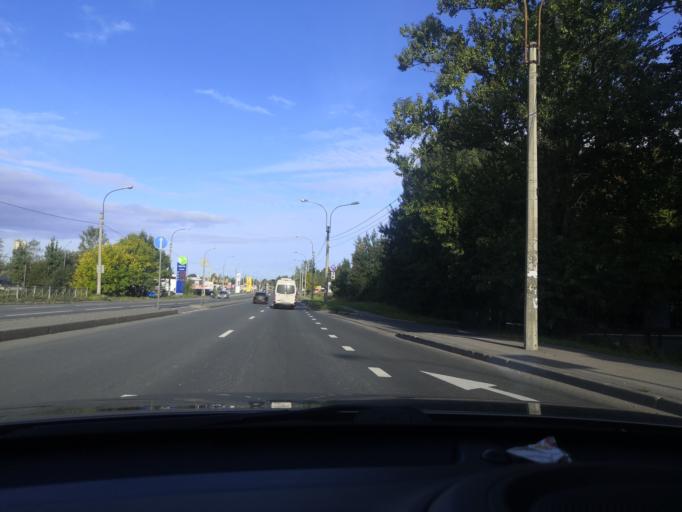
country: RU
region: St.-Petersburg
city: Pargolovo
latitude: 60.0761
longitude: 30.2744
